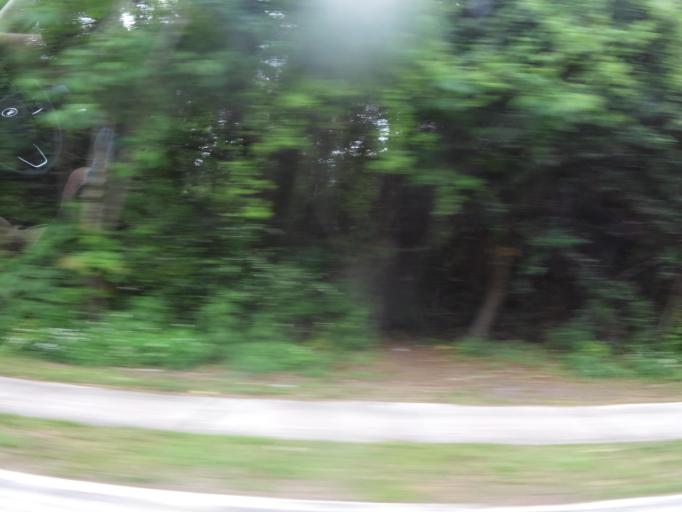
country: US
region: Florida
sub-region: Duval County
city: Jacksonville
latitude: 30.3024
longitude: -81.7466
